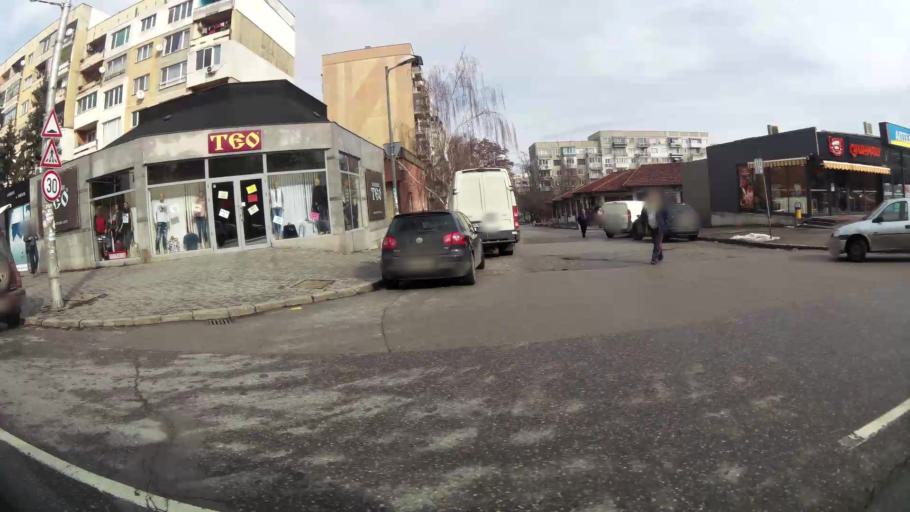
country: BG
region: Sofiya
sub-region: Obshtina Bozhurishte
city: Bozhurishte
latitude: 42.7206
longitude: 23.2427
